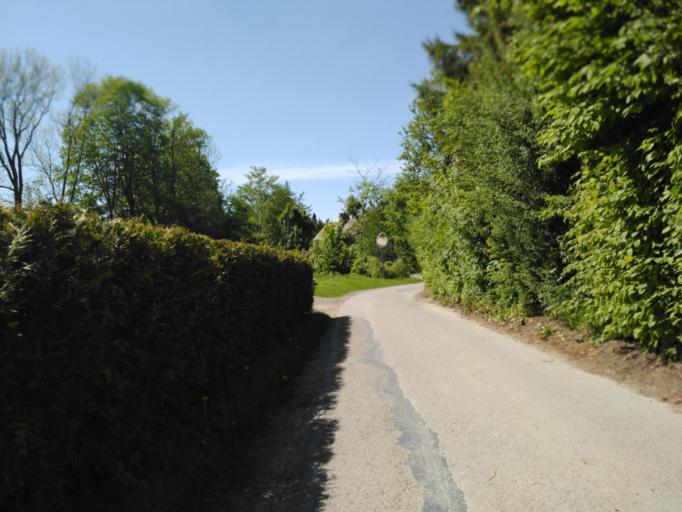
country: PL
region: Subcarpathian Voivodeship
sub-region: Powiat krosnienski
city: Iwonicz-Zdroj
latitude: 49.5972
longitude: 21.7969
